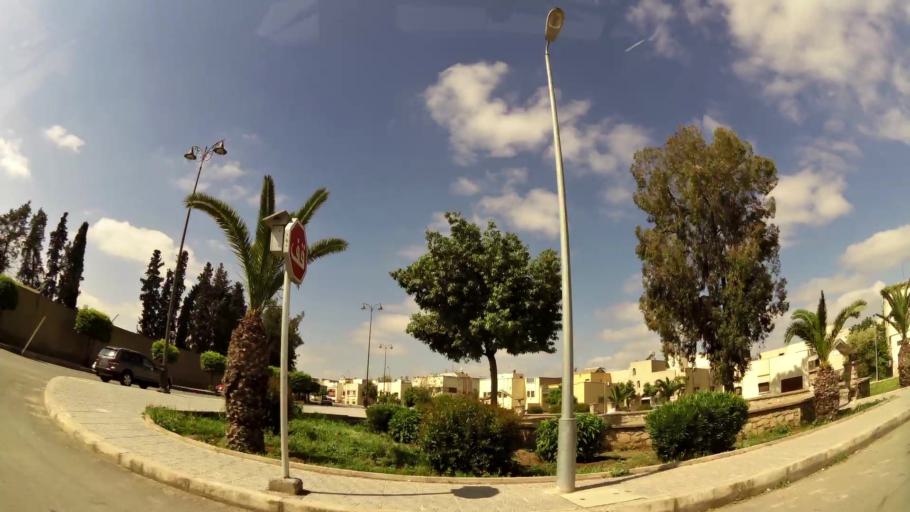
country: MA
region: Fes-Boulemane
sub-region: Fes
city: Fes
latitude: 34.0316
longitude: -5.0222
